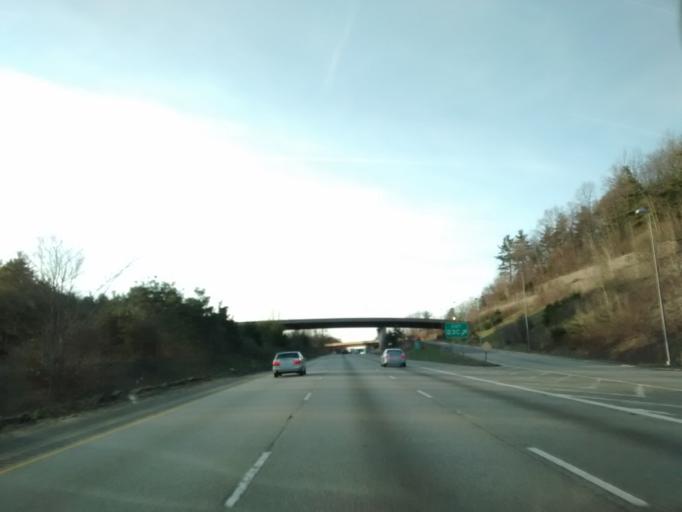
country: US
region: Massachusetts
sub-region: Middlesex County
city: Marlborough
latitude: 42.3185
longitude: -71.5699
